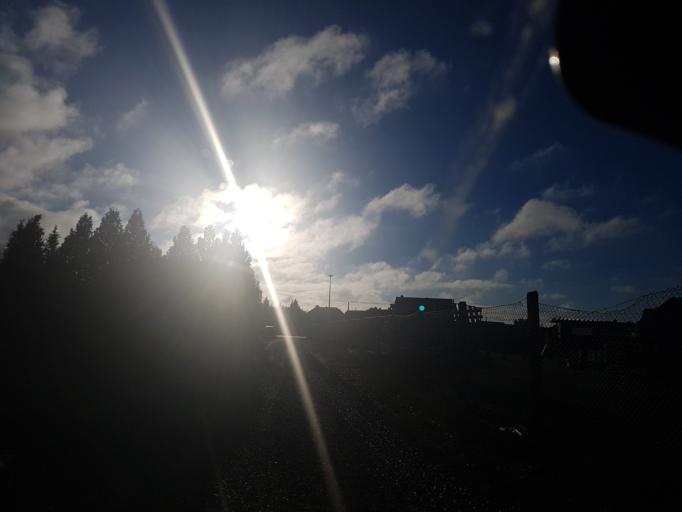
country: DE
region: Brandenburg
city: Schonborn
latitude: 51.5427
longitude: 13.4690
